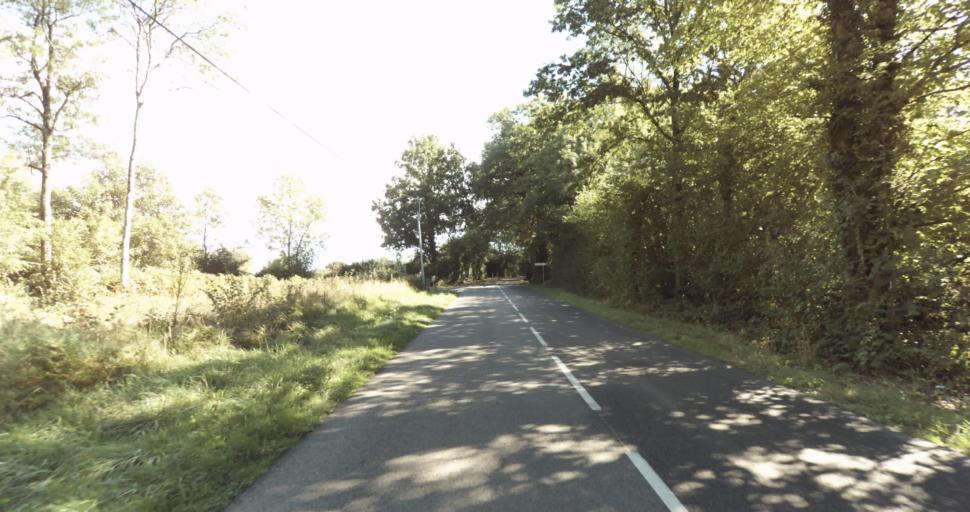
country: FR
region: Lower Normandy
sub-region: Departement de l'Orne
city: Gace
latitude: 48.7881
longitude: 0.2346
